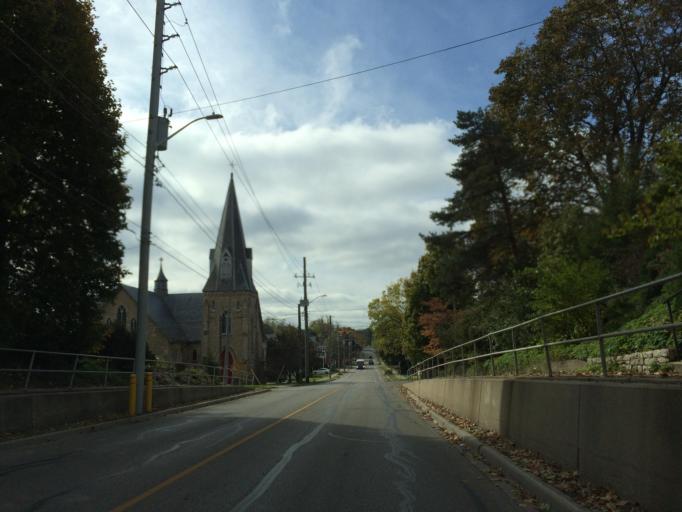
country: CA
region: Ontario
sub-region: Wellington County
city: Guelph
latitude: 43.5440
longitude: -80.2558
